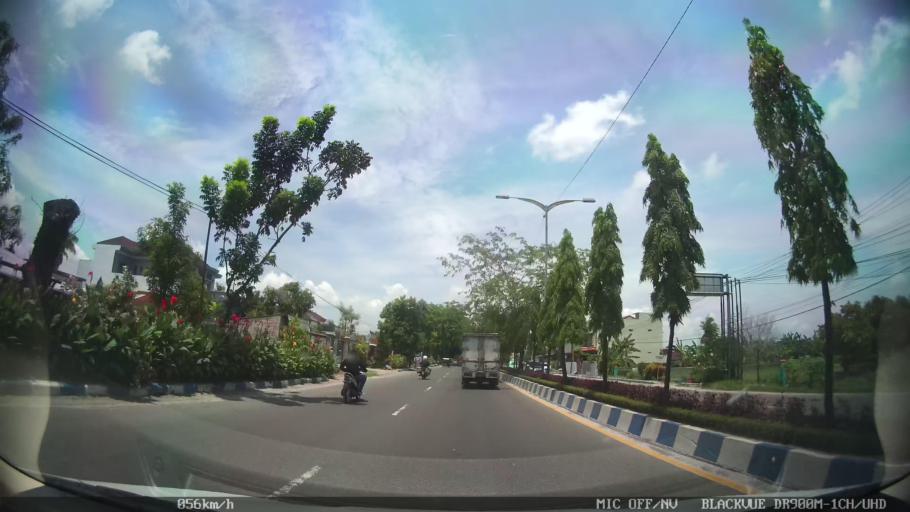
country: ID
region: North Sumatra
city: Percut
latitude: 3.5519
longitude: 98.8619
